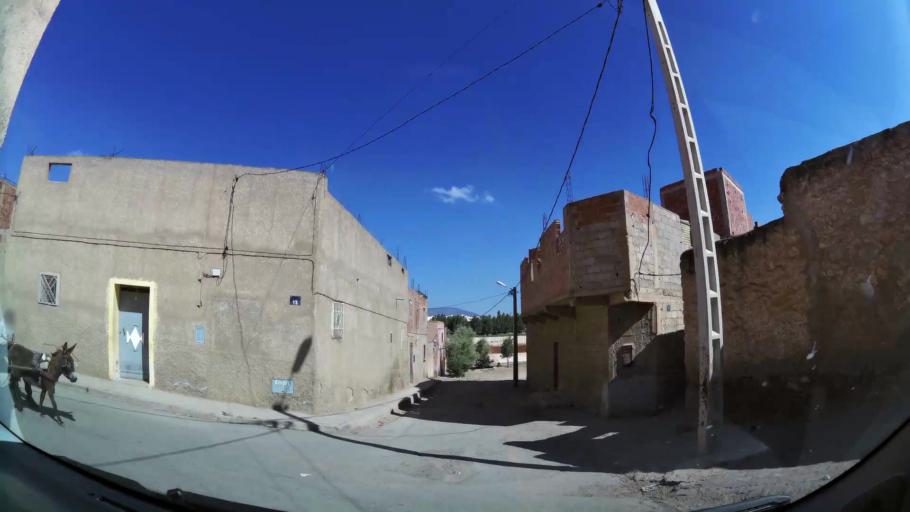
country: MA
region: Oriental
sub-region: Oujda-Angad
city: Oujda
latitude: 34.6885
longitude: -1.9282
